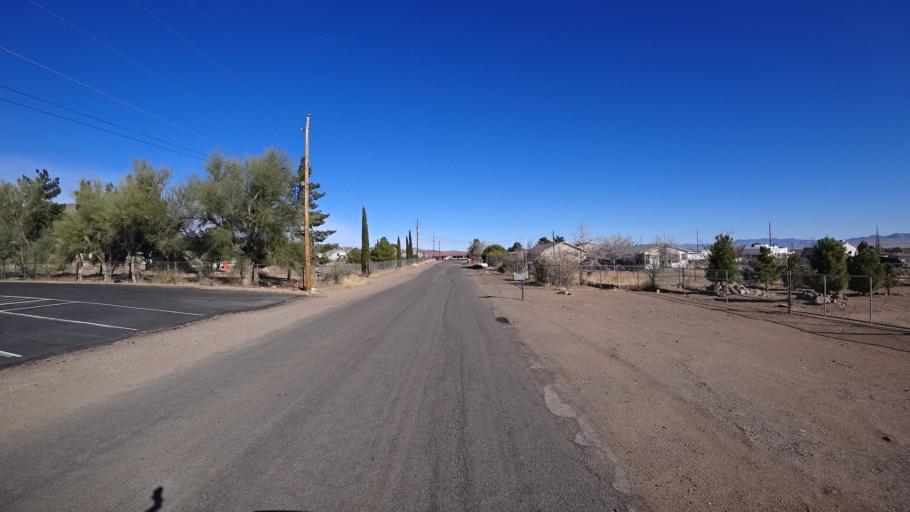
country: US
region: Arizona
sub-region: Mohave County
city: New Kingman-Butler
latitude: 35.2519
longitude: -114.0350
